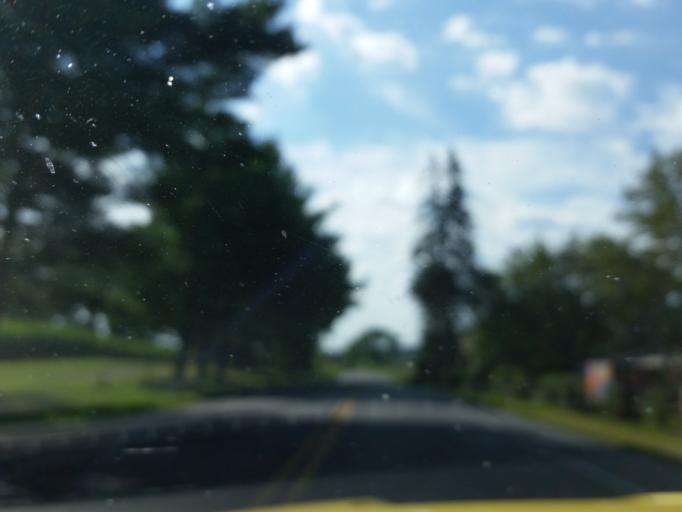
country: US
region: Pennsylvania
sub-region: Lebanon County
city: Sand Hill
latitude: 40.3884
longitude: -76.4140
